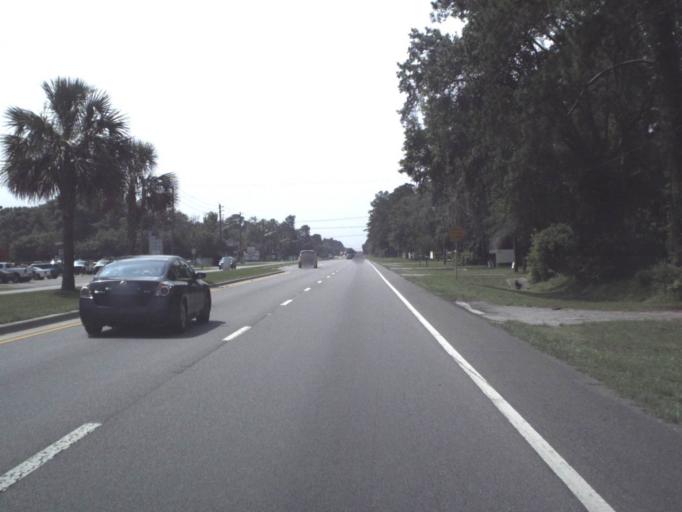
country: US
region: Florida
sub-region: Duval County
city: Jacksonville
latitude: 30.4056
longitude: -81.7439
